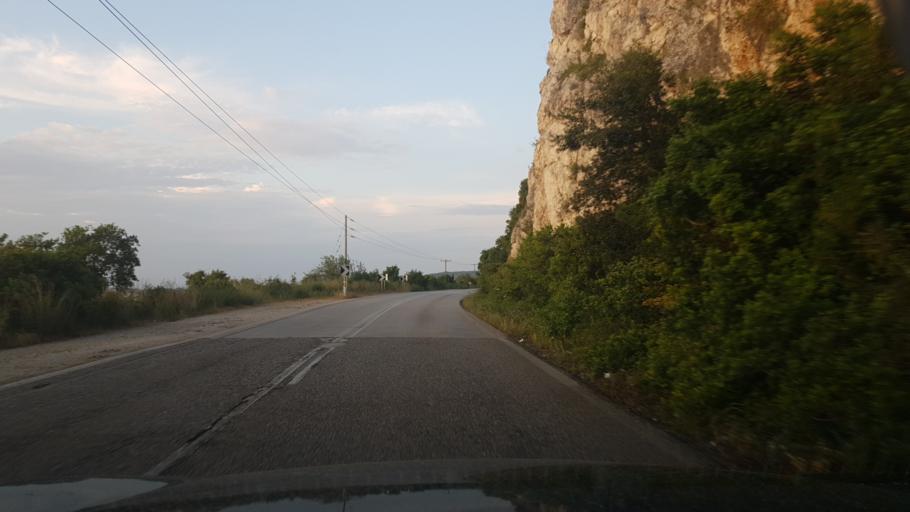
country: GR
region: Ionian Islands
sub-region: Lefkada
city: Lefkada
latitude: 38.8574
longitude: 20.7512
